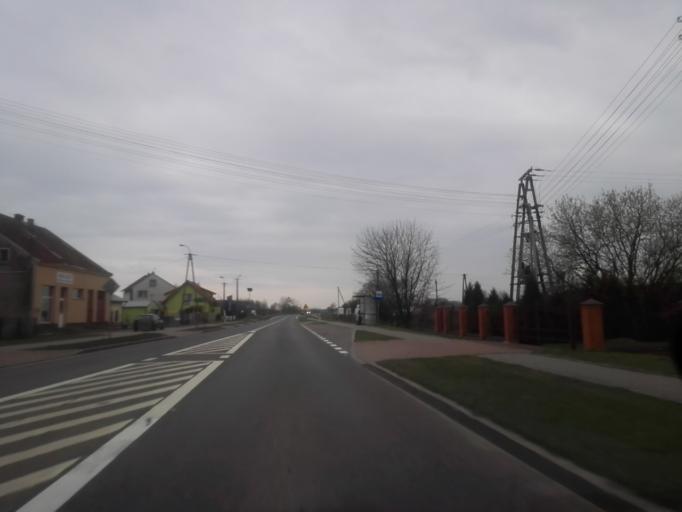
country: PL
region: Podlasie
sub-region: Powiat grajewski
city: Rajgrod
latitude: 53.6838
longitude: 22.6190
